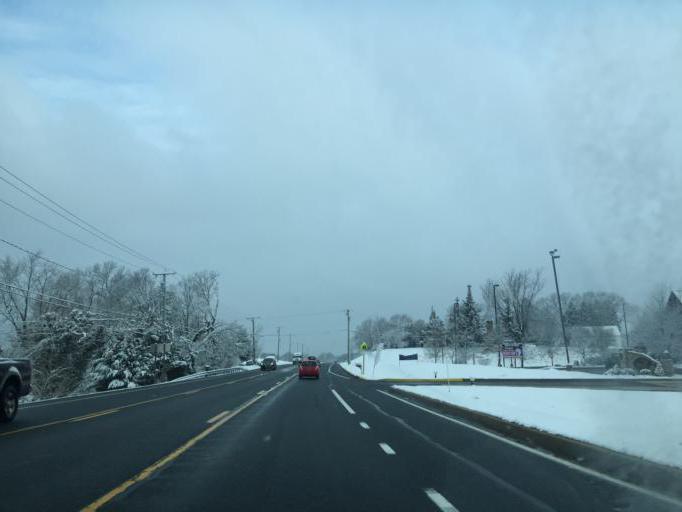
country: US
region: Maryland
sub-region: Harford County
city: Joppatowne
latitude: 39.4660
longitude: -76.3697
